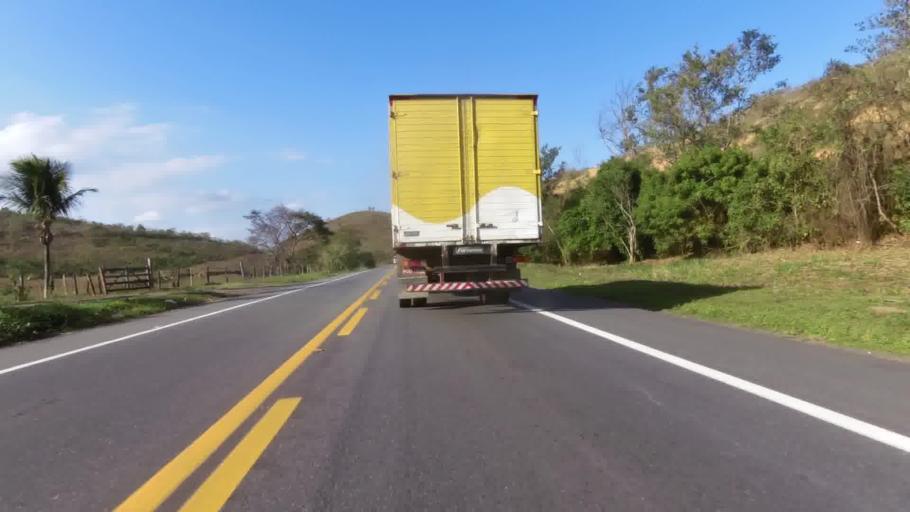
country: BR
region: Espirito Santo
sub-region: Mimoso Do Sul
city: Mimoso do Sul
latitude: -21.1688
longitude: -41.2892
